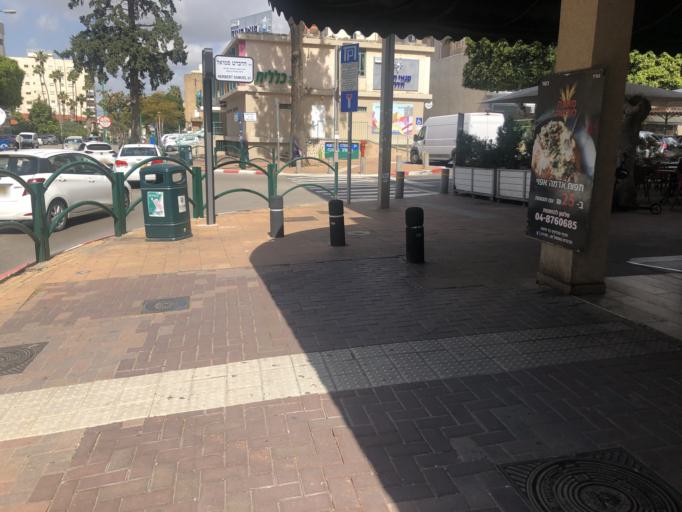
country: IL
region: Haifa
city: Hadera
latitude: 32.4369
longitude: 34.9171
